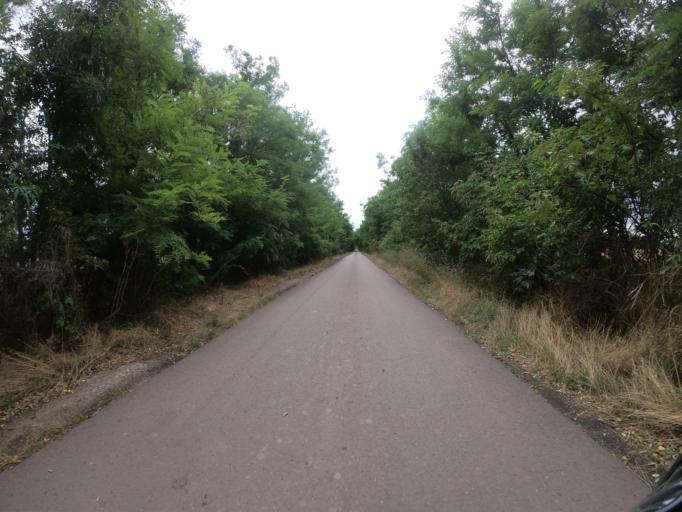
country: HU
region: Borsod-Abauj-Zemplen
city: Szentistvan
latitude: 47.7303
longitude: 20.6844
